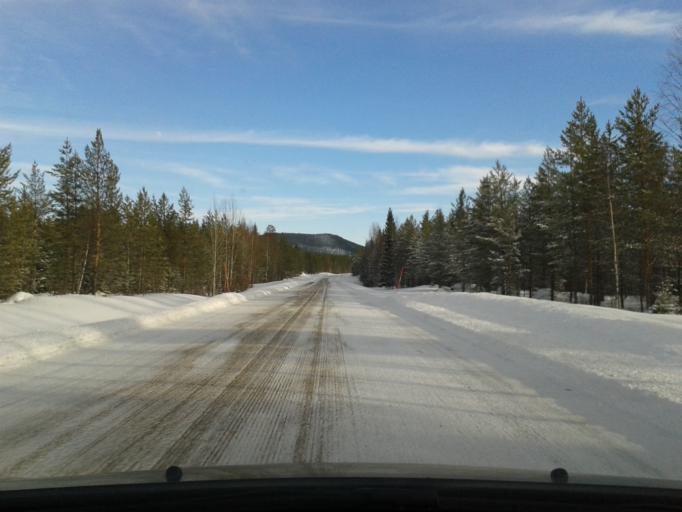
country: SE
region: Vaesterbotten
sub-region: Asele Kommun
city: Asele
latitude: 64.3165
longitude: 17.1505
